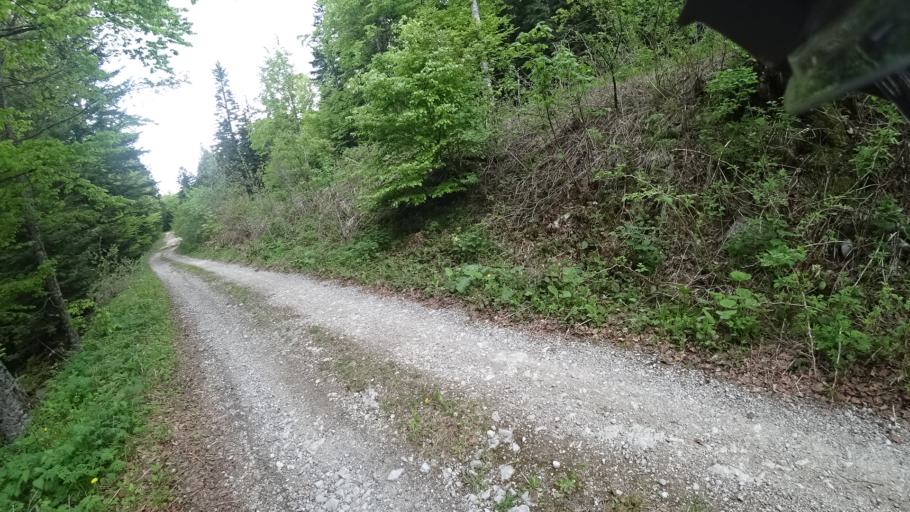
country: HR
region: Karlovacka
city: Plaski
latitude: 44.9184
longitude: 15.4281
